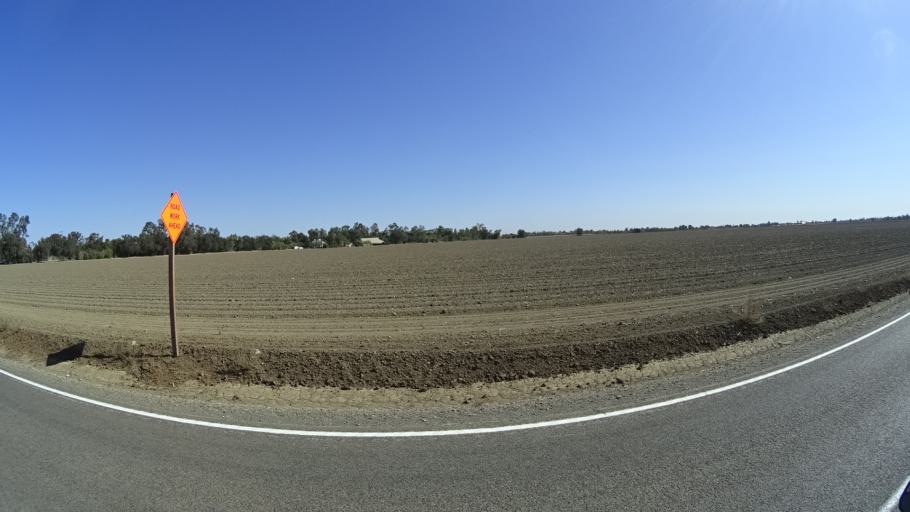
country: US
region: California
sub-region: Yolo County
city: Winters
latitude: 38.5595
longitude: -121.8591
